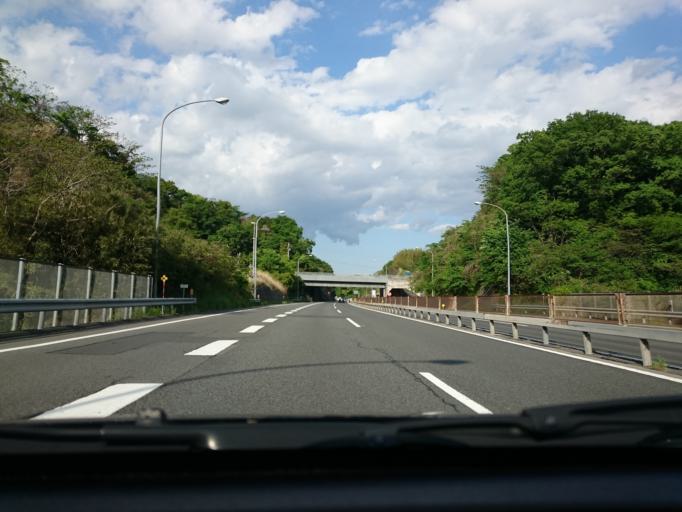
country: JP
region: Kanagawa
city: Ninomiya
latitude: 35.3195
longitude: 139.2722
